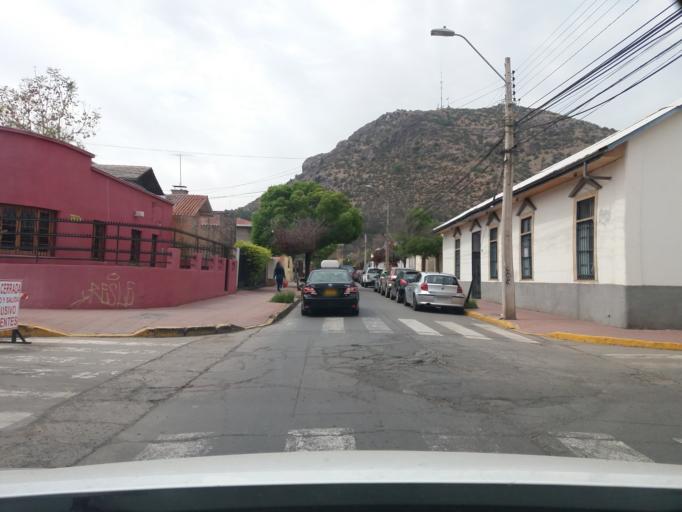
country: CL
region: Valparaiso
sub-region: Provincia de Los Andes
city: Los Andes
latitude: -32.8351
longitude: -70.5954
